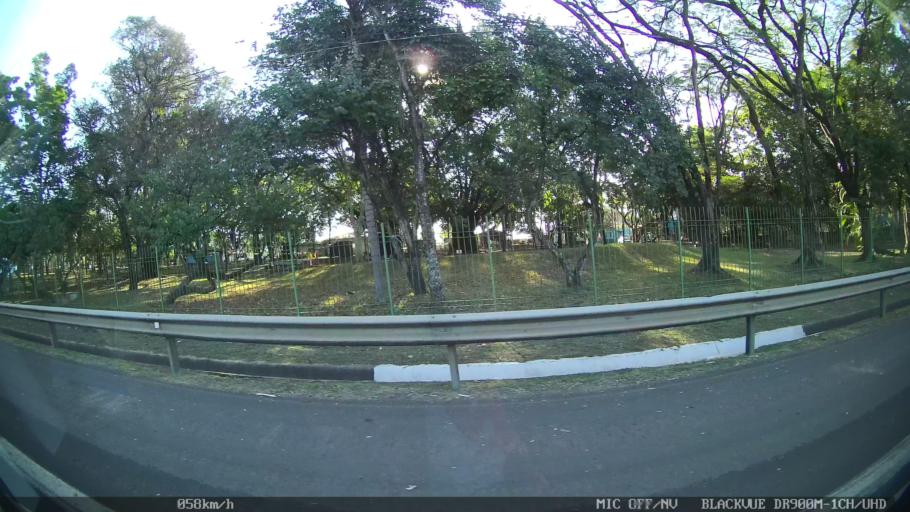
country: BR
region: Sao Paulo
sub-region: Piracicaba
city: Piracicaba
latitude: -22.6957
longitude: -47.6511
